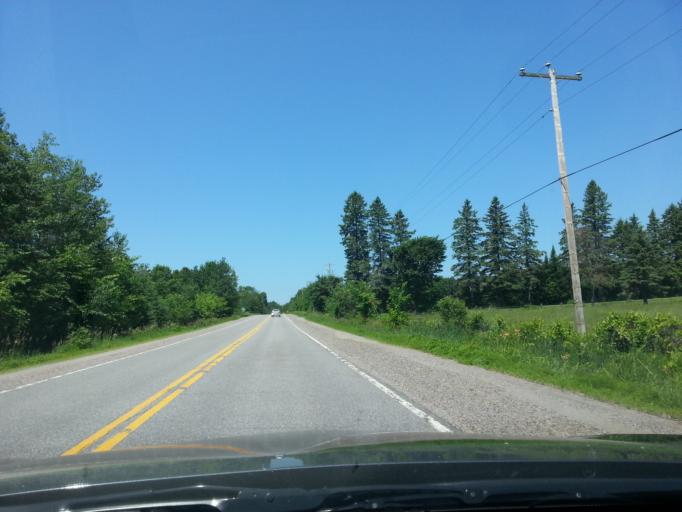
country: CA
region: Ontario
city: Arnprior
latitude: 45.5468
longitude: -76.3483
